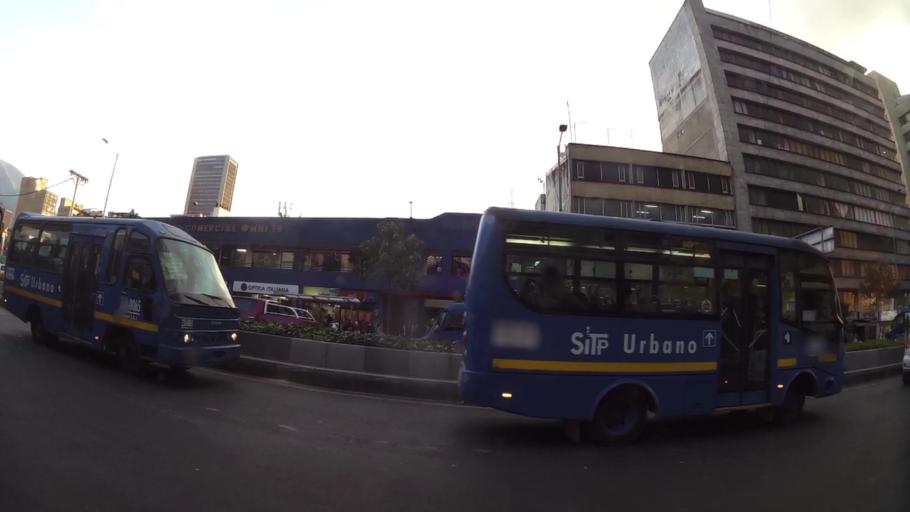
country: CO
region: Bogota D.C.
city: Bogota
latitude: 4.6061
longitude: -74.0725
